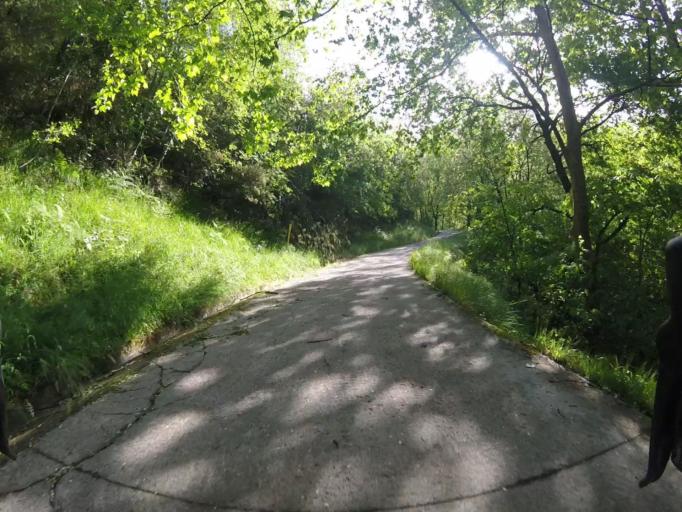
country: ES
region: Basque Country
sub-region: Provincia de Guipuzcoa
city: Andoain
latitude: 43.2031
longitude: -2.0060
